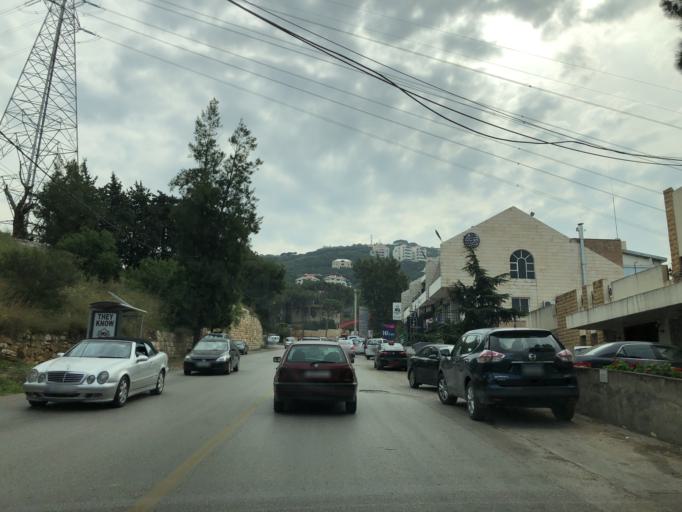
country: LB
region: Mont-Liban
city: Jdaidet el Matn
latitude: 33.8551
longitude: 35.5841
